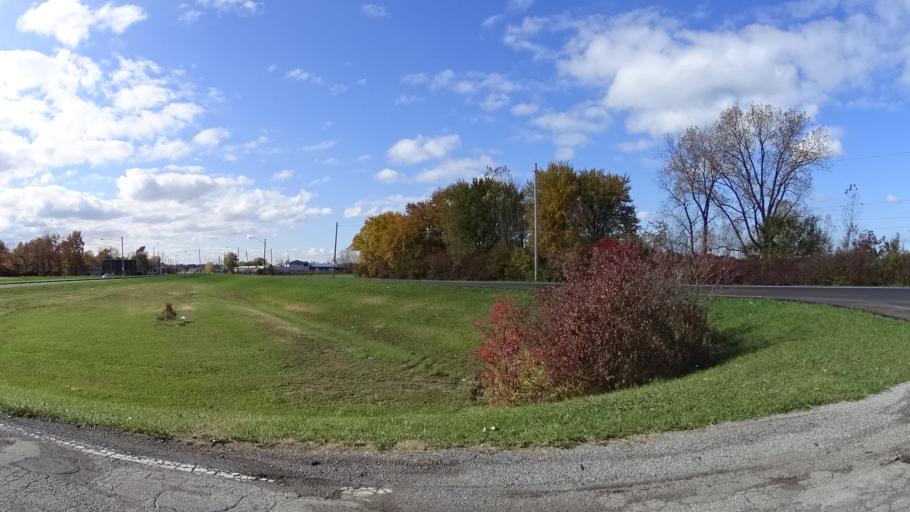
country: US
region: Ohio
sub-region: Lorain County
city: Lorain
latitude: 41.4461
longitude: -82.2260
